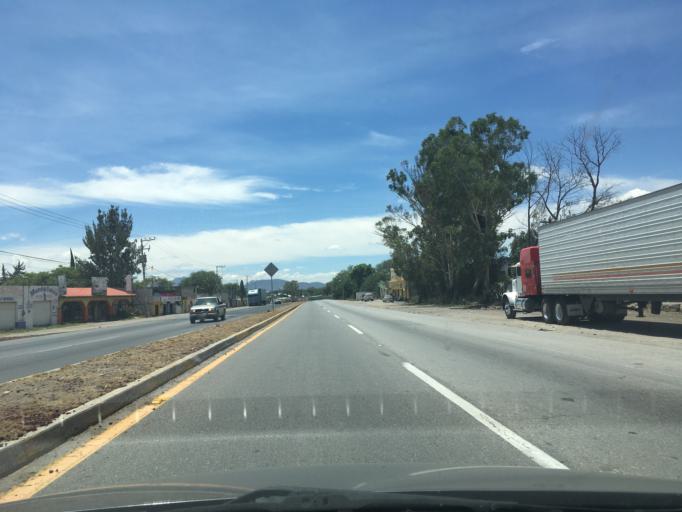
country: MX
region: Hidalgo
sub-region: Tasquillo
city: Portezuelo
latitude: 20.4821
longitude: -99.2857
